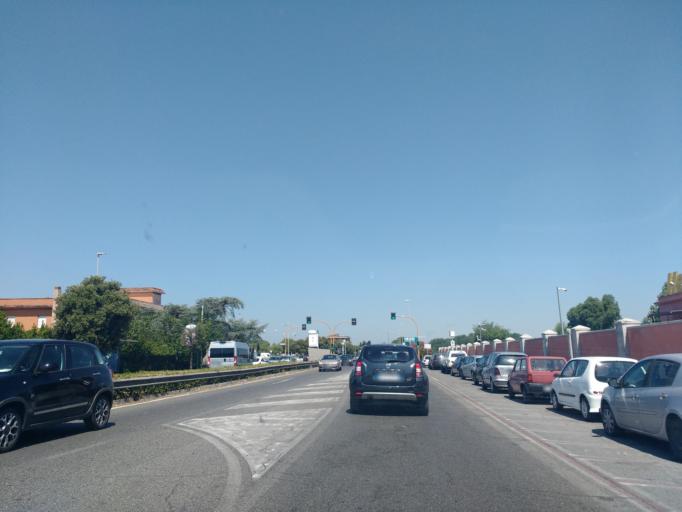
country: IT
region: Latium
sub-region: Citta metropolitana di Roma Capitale
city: Fiumicino-Isola Sacra
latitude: 41.7653
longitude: 12.2641
